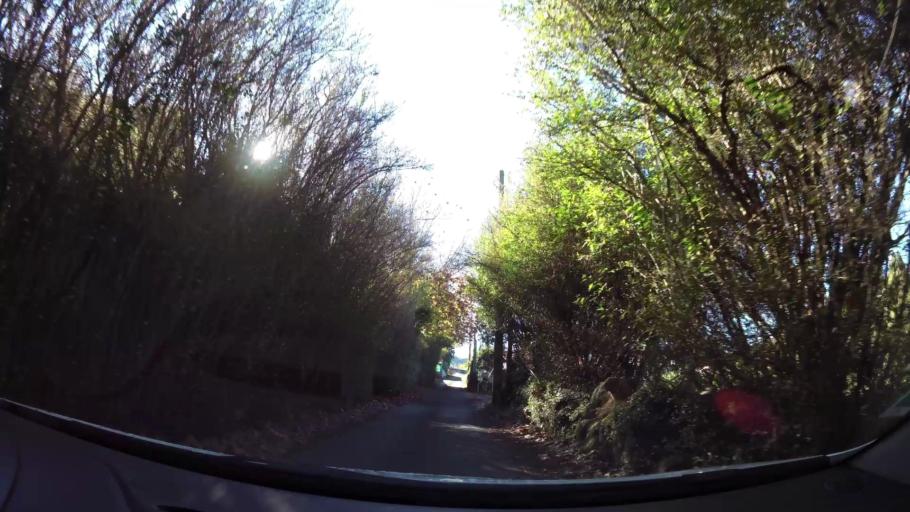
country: RE
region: Reunion
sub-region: Reunion
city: Le Tampon
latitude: -21.2202
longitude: 55.5603
